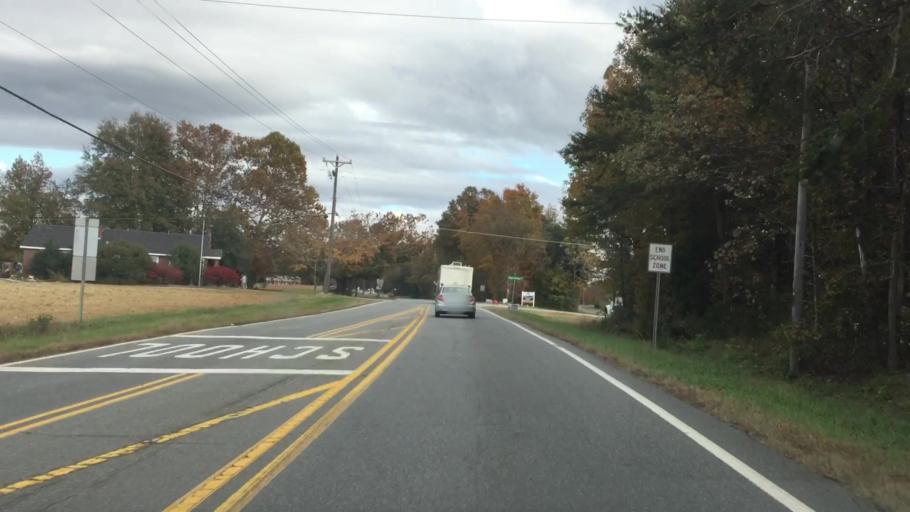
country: US
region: North Carolina
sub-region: Guilford County
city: Stokesdale
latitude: 36.2349
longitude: -79.9758
